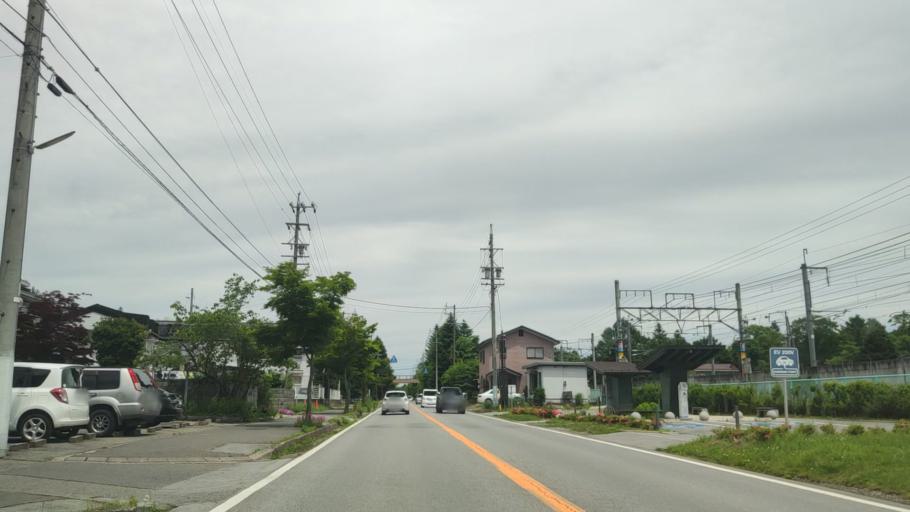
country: JP
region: Nagano
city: Saku
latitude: 36.3438
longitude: 138.6132
